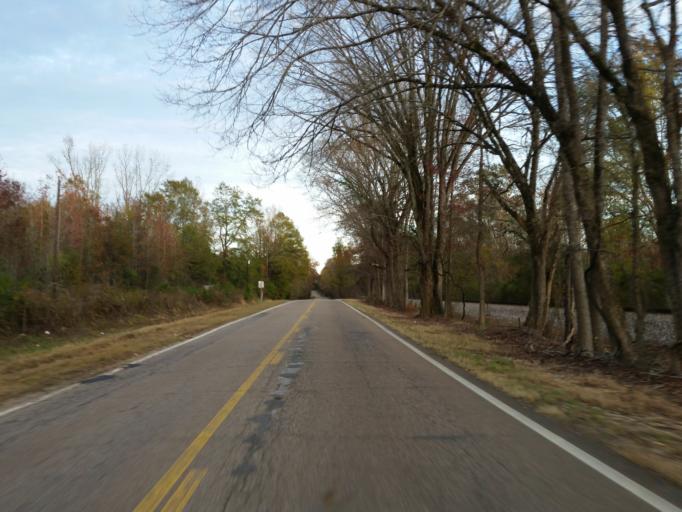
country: US
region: Alabama
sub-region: Sumter County
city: York
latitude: 32.4239
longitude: -88.4312
